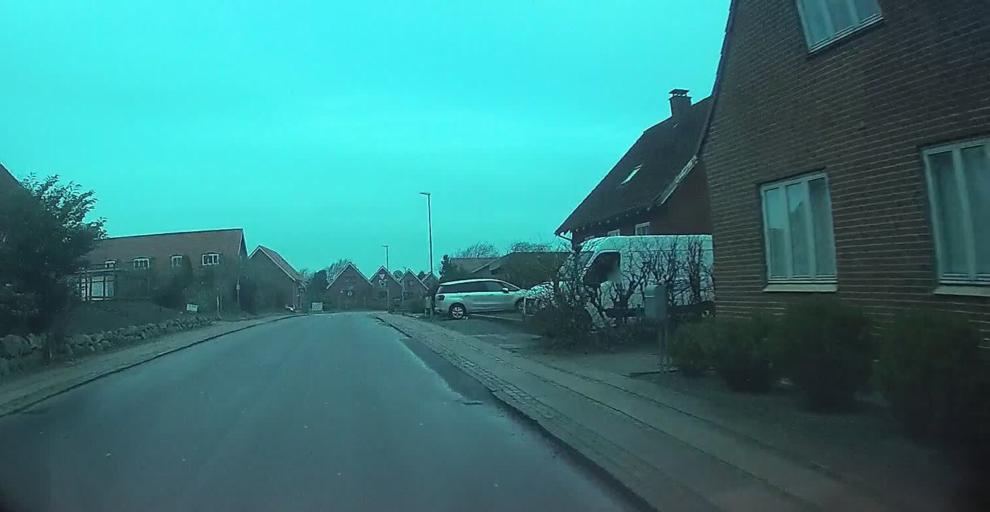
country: DK
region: North Denmark
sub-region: Thisted Kommune
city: Hurup
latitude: 56.7514
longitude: 8.4241
